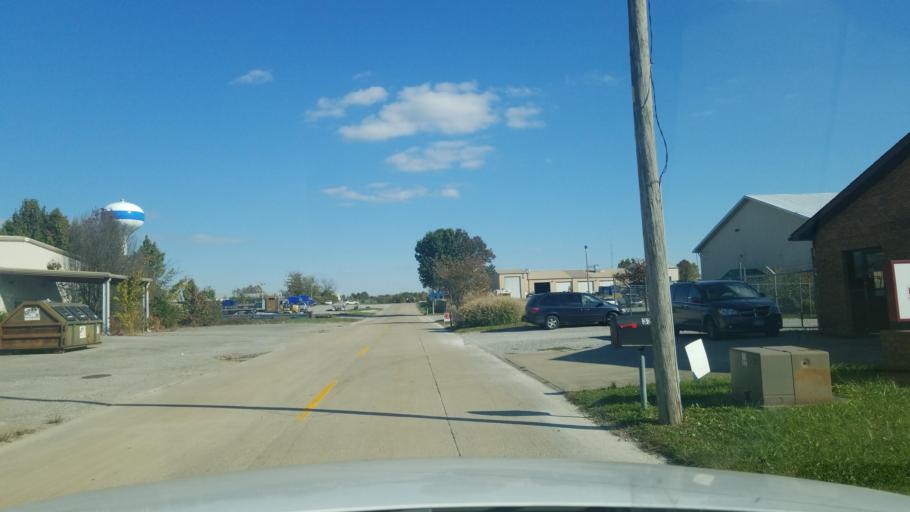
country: US
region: Illinois
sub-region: Williamson County
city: Energy
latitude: 37.7397
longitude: -88.9875
